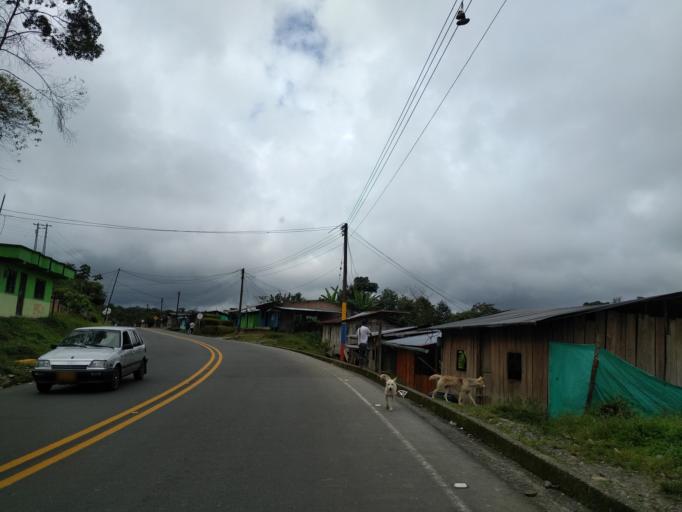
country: CO
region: Narino
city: Ricaurte
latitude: 1.3615
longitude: -78.1839
